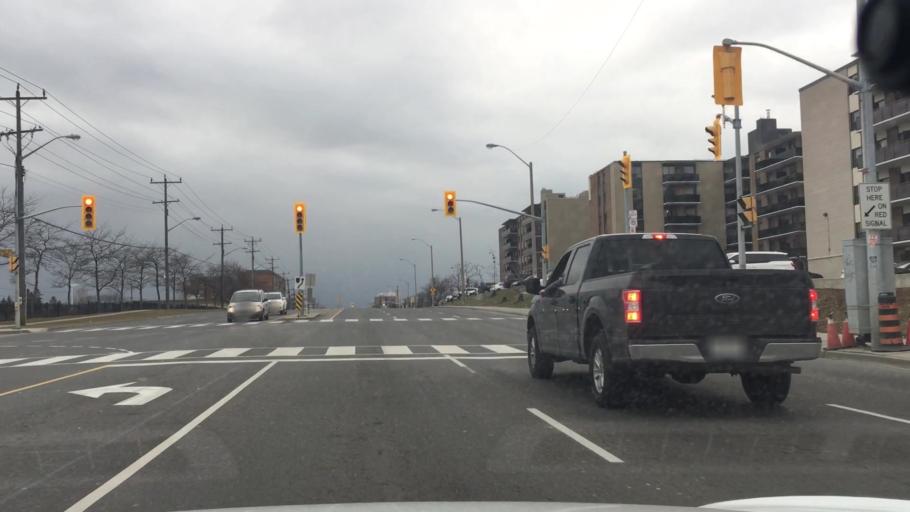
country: CA
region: Ontario
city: Scarborough
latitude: 43.7589
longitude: -79.2312
